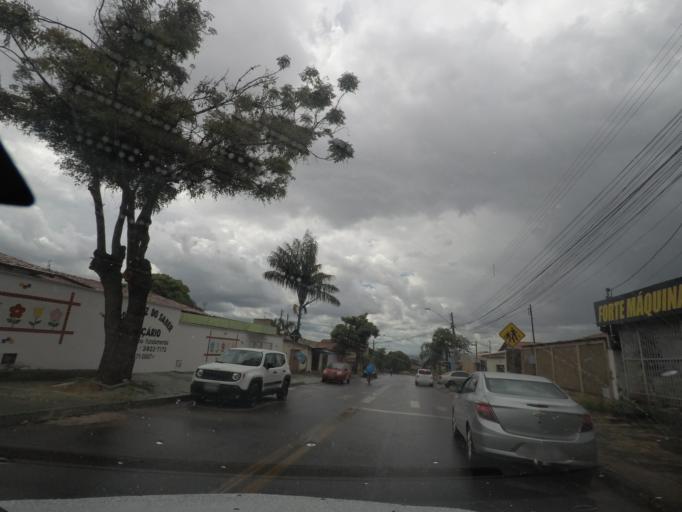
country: BR
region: Goias
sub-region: Goiania
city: Goiania
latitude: -16.7494
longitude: -49.3234
